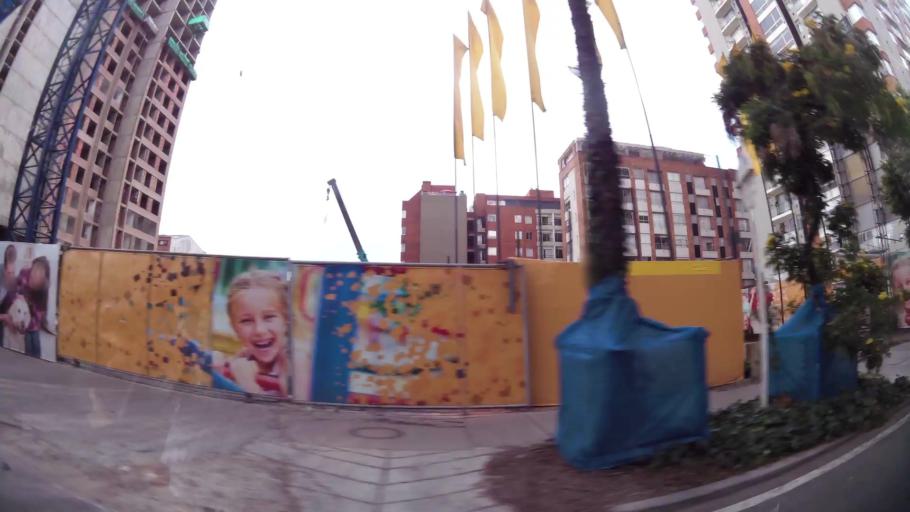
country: CO
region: Bogota D.C.
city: Barrio San Luis
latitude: 4.7259
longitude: -74.0331
